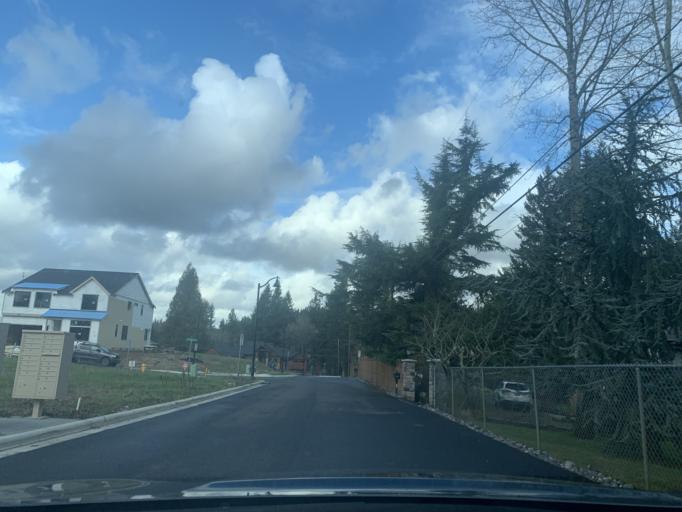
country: US
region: Oregon
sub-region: Washington County
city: Cedar Mill
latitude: 45.5490
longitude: -122.8002
